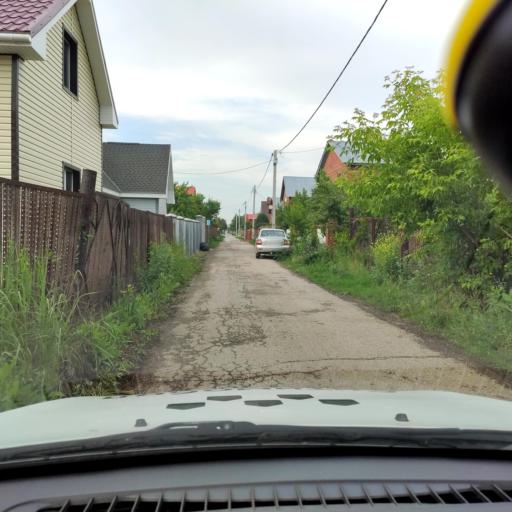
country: RU
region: Samara
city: Podstepki
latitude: 53.5778
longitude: 49.0794
